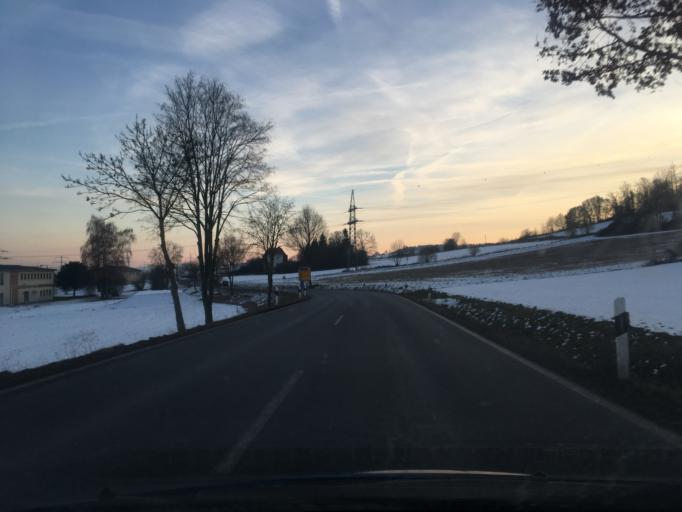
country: DE
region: Lower Saxony
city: Hardegsen
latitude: 51.6508
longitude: 9.8491
